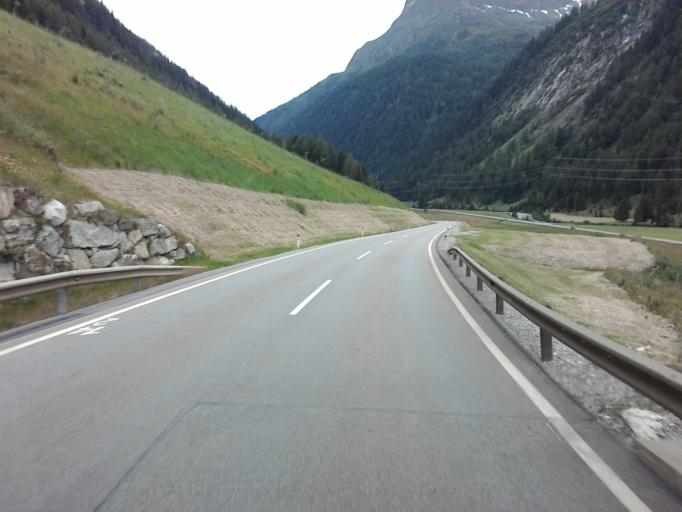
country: AT
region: Tyrol
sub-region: Politischer Bezirk Lienz
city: Matrei in Osttirol
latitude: 47.1152
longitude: 12.5040
